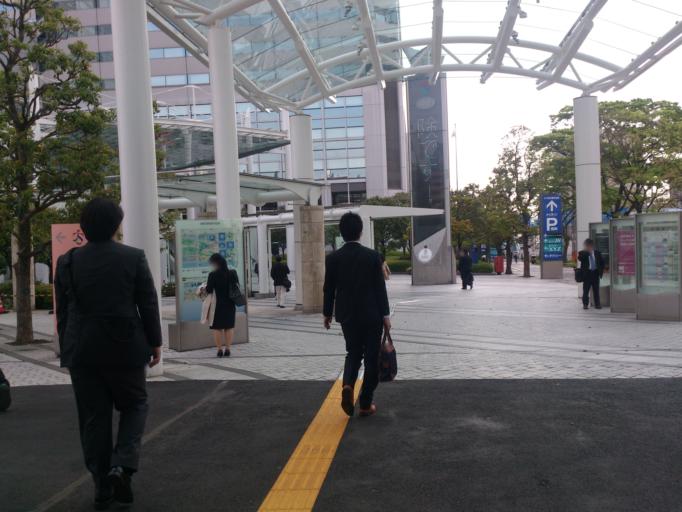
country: JP
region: Tokyo
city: Tokyo
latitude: 35.6570
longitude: 139.7804
